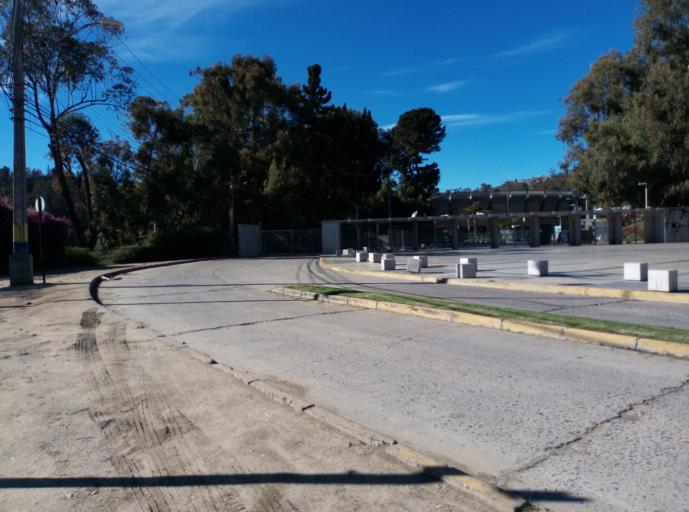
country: CL
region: Valparaiso
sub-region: Provincia de Valparaiso
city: Vina del Mar
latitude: -33.0147
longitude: -71.5375
